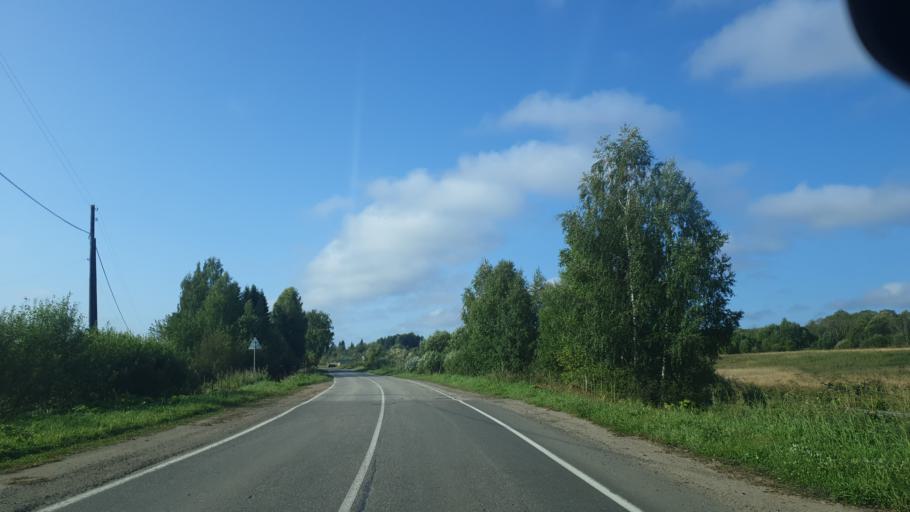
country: RU
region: Komi Republic
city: Vizinga
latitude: 60.9313
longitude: 50.2247
